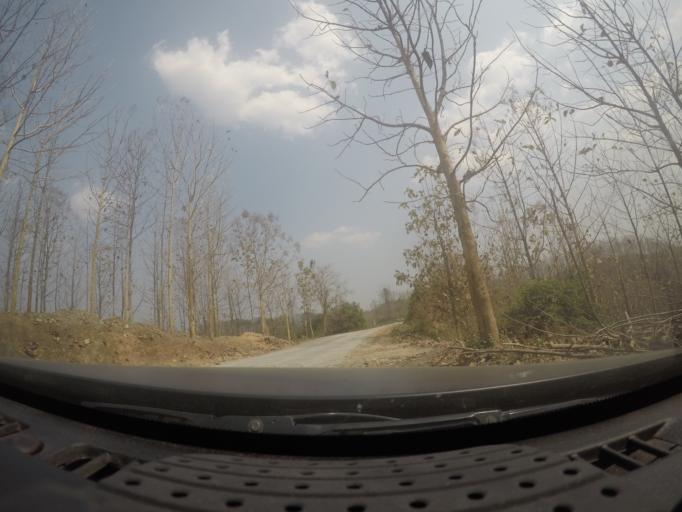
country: MM
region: Magway
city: Taungdwingyi
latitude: 19.9491
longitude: 95.7710
